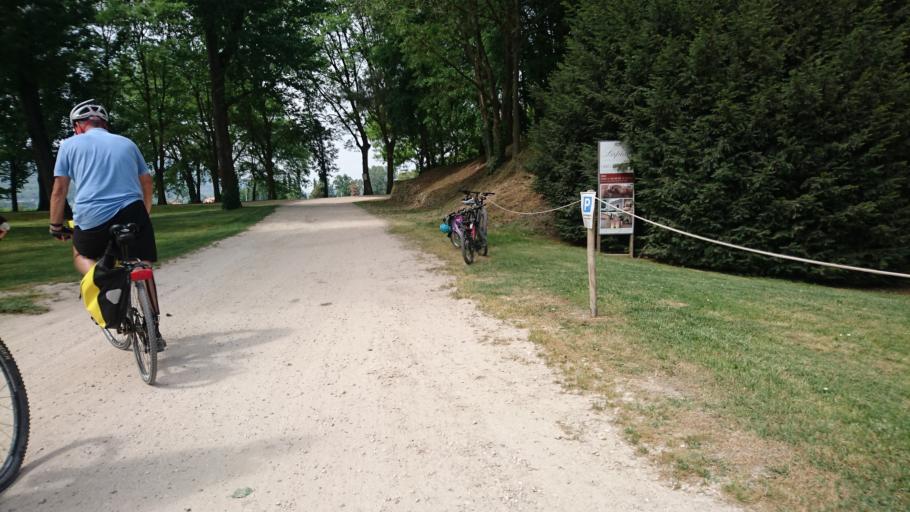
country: IT
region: Veneto
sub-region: Provincia di Padova
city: Battaglia Terme
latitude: 45.2817
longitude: 11.7626
